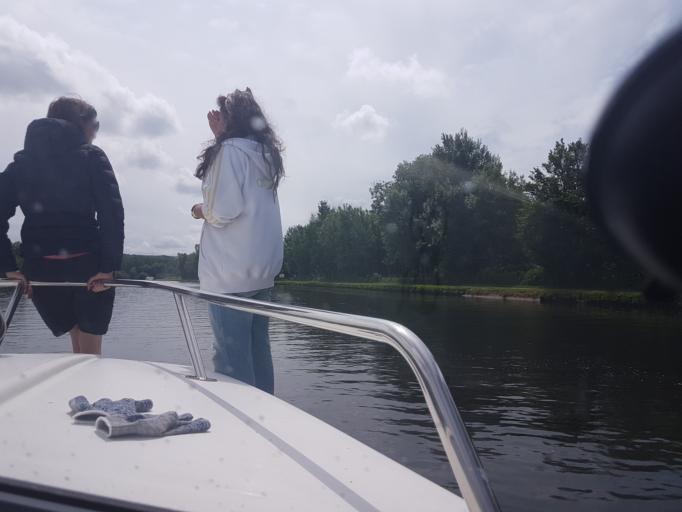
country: FR
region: Bourgogne
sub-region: Departement de l'Yonne
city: Augy
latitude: 47.7810
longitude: 3.6018
